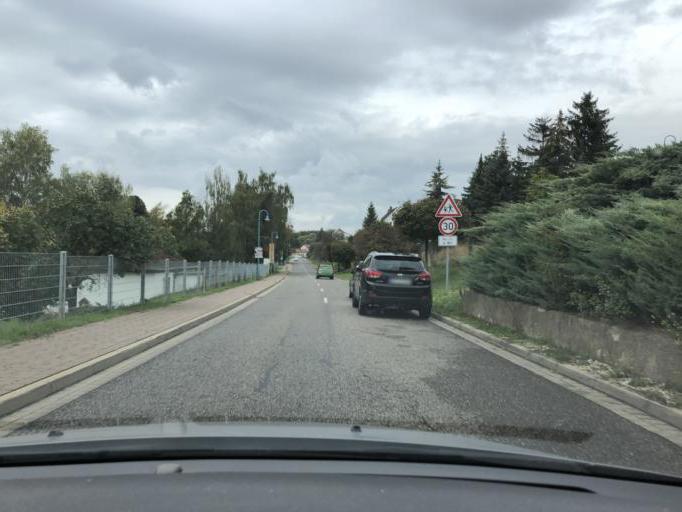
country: DE
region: Saxony-Anhalt
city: Uichteritz
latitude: 51.2090
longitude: 11.9198
